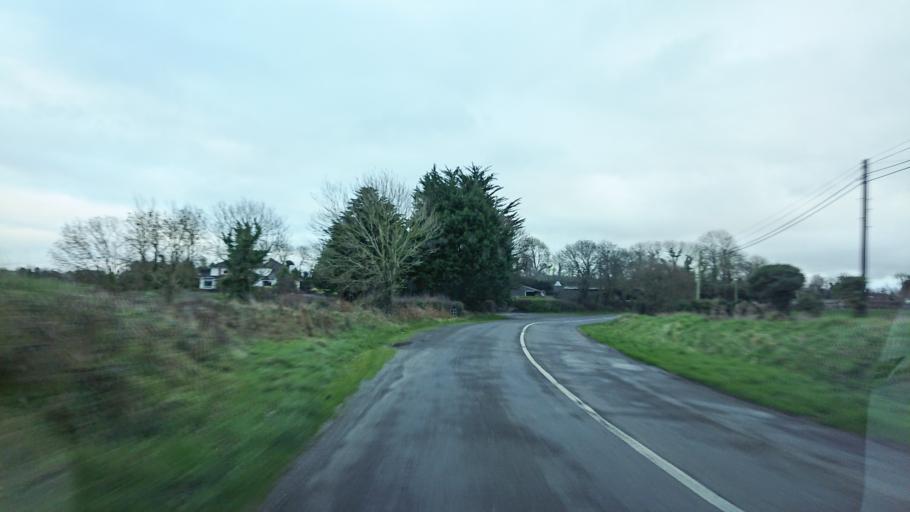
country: IE
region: Munster
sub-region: Waterford
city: Portlaw
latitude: 52.1895
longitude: -7.4108
